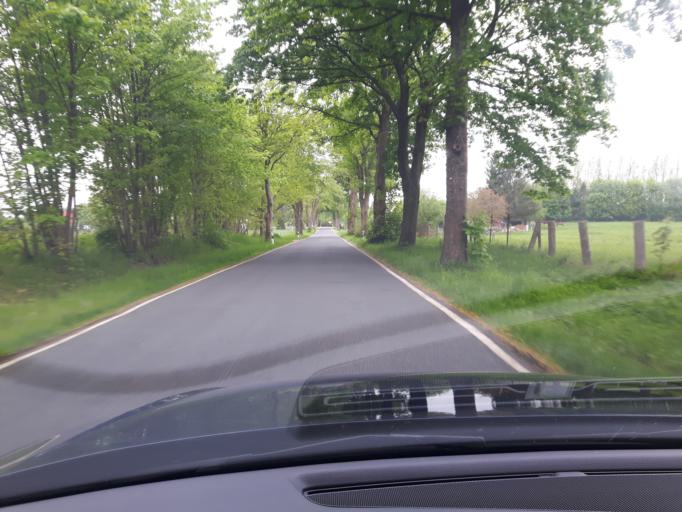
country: DE
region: Mecklenburg-Vorpommern
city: Velgast
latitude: 54.2001
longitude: 12.7310
